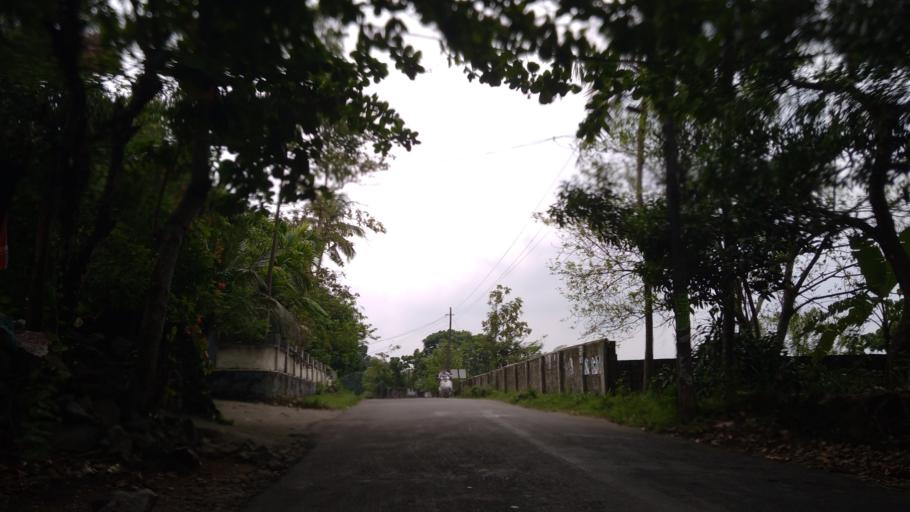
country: IN
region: Kerala
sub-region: Ernakulam
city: Kotamangalam
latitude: 10.1217
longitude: 76.5741
